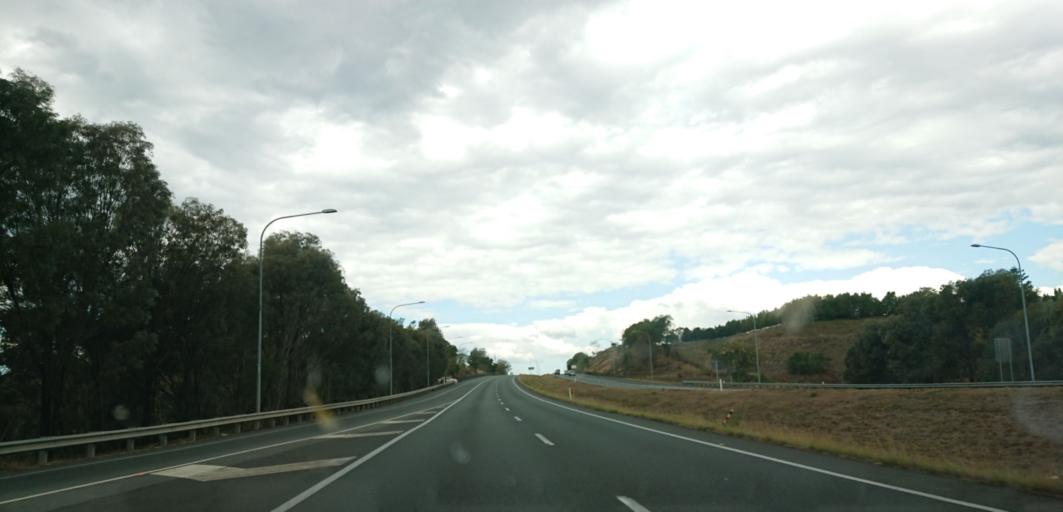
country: AU
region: Queensland
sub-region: Ipswich
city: Thagoona
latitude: -27.5633
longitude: 152.5983
